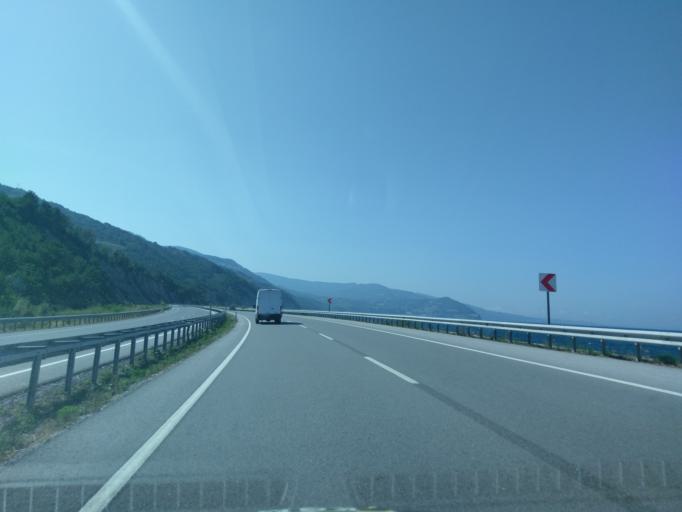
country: TR
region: Sinop
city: Dikmen
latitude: 41.7010
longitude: 35.3387
